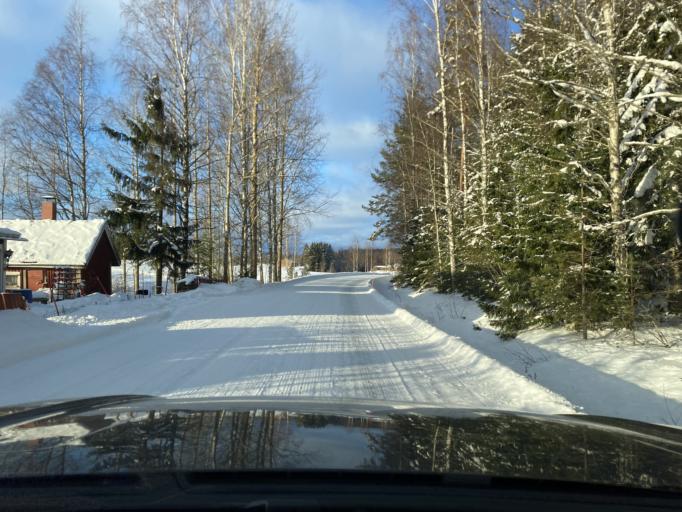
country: FI
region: Pirkanmaa
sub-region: Lounais-Pirkanmaa
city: Punkalaidun
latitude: 61.0704
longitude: 23.2197
